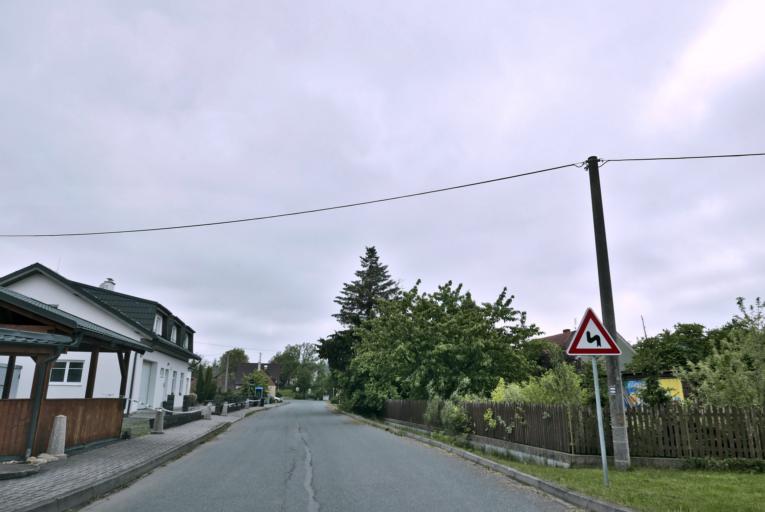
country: CZ
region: Plzensky
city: Kralovice
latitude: 49.9447
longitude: 13.4655
